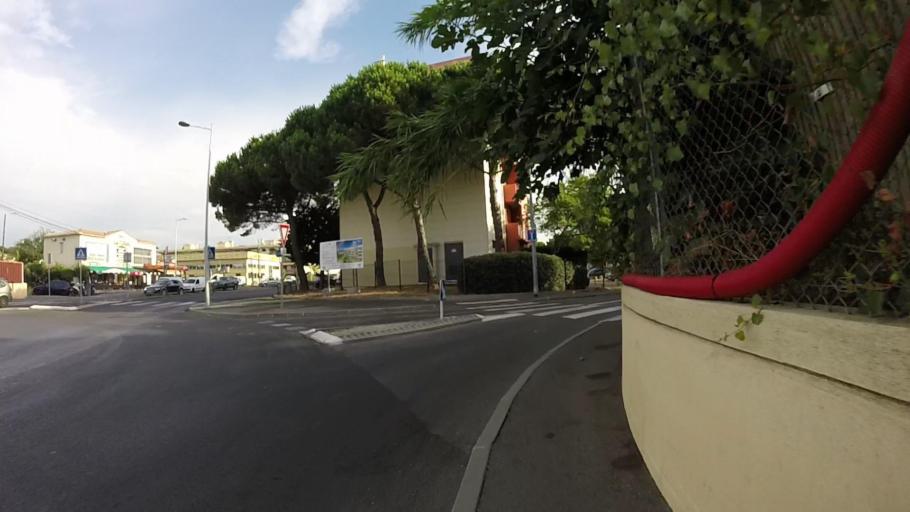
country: FR
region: Provence-Alpes-Cote d'Azur
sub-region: Departement des Alpes-Maritimes
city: Biot
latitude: 43.6003
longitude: 7.1132
